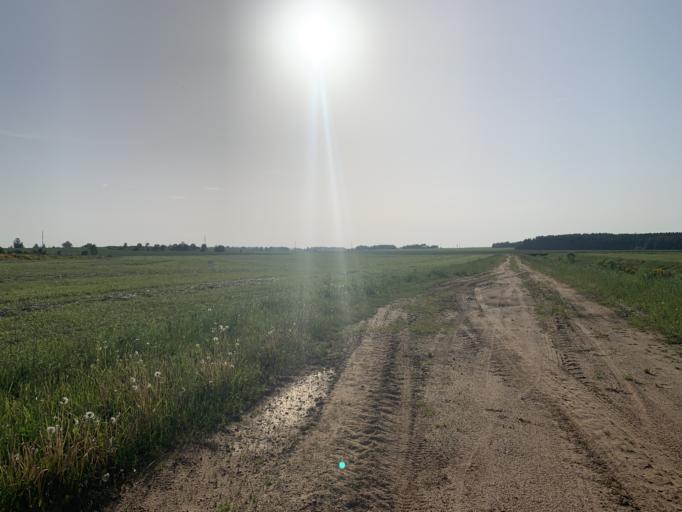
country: BY
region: Minsk
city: Kapyl'
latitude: 53.2428
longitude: 26.9537
